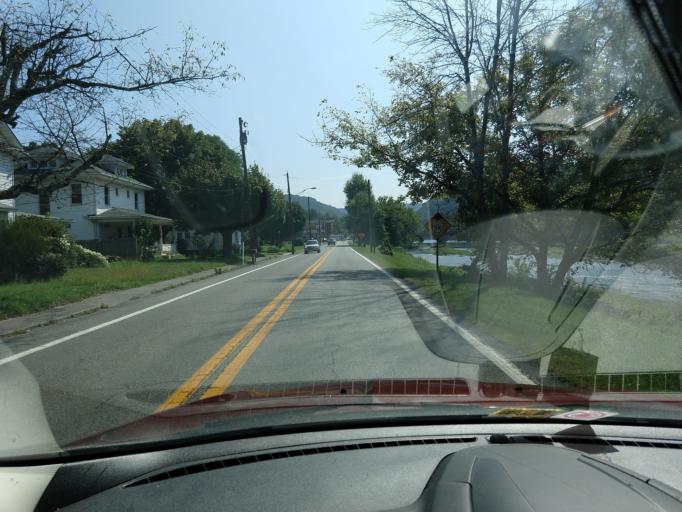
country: US
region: West Virginia
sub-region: Greenbrier County
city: Alderson
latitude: 37.7264
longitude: -80.6453
